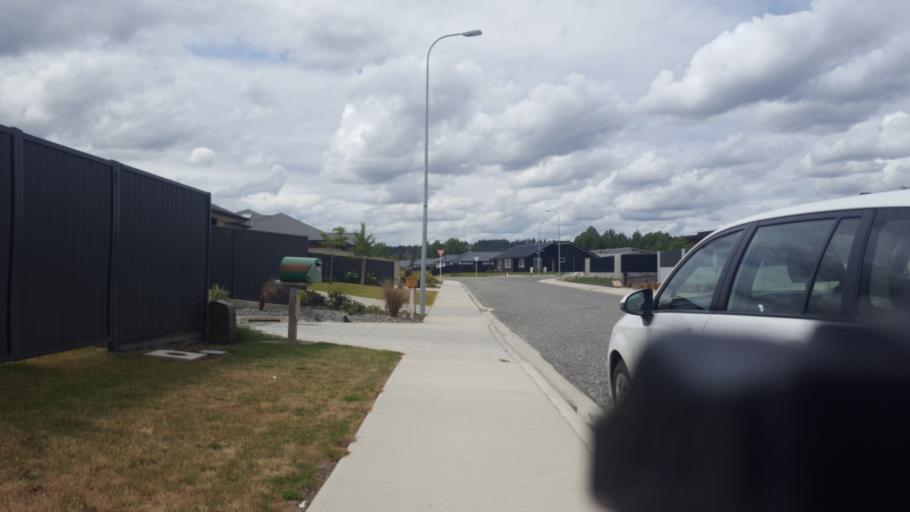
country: NZ
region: Otago
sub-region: Queenstown-Lakes District
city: Wanaka
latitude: -45.2437
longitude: 169.3740
